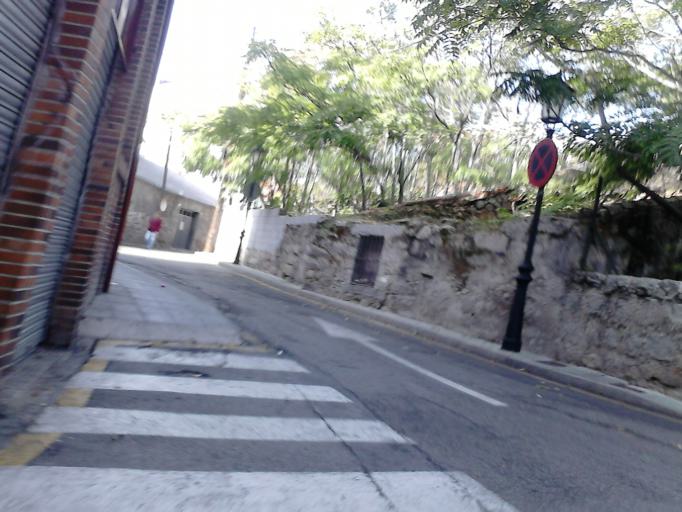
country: ES
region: Madrid
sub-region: Provincia de Madrid
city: Galapagar
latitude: 40.5774
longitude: -4.0027
